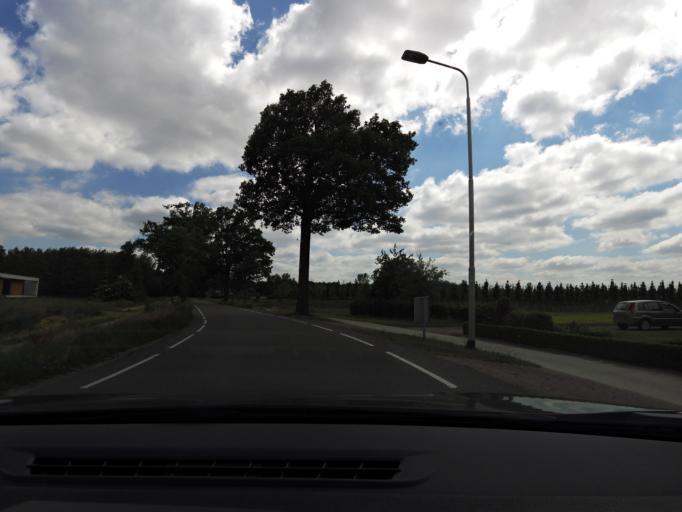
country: NL
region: North Brabant
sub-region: Gemeente Loon op Zand
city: Loon op Zand
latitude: 51.6228
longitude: 5.1230
